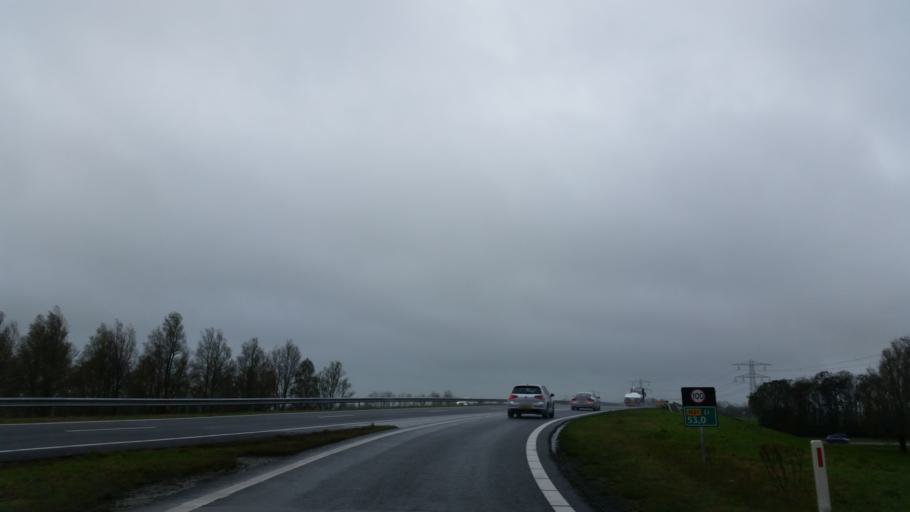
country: NL
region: Friesland
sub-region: Gemeente Boarnsterhim
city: Wergea
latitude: 53.1678
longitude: 5.8324
